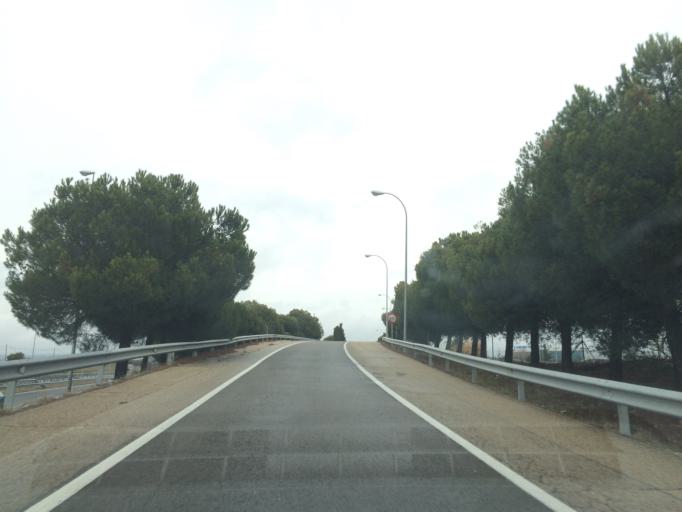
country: ES
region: Madrid
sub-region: Provincia de Madrid
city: Tres Cantos
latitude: 40.6005
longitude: -3.7196
